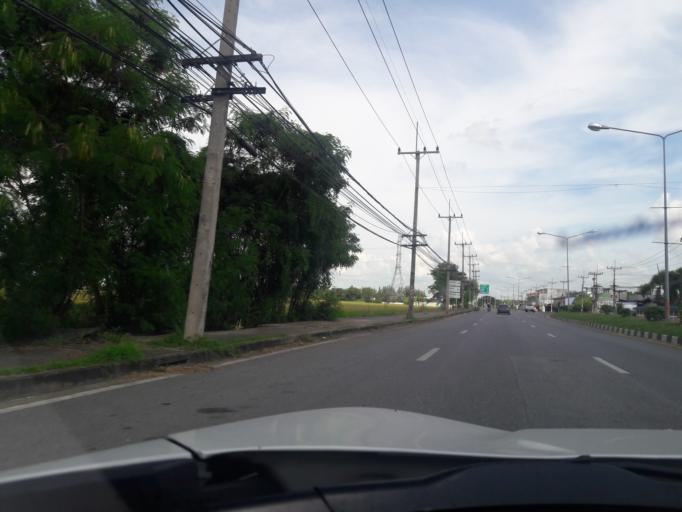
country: TH
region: Lop Buri
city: Ban Mi
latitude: 15.0454
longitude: 100.5532
